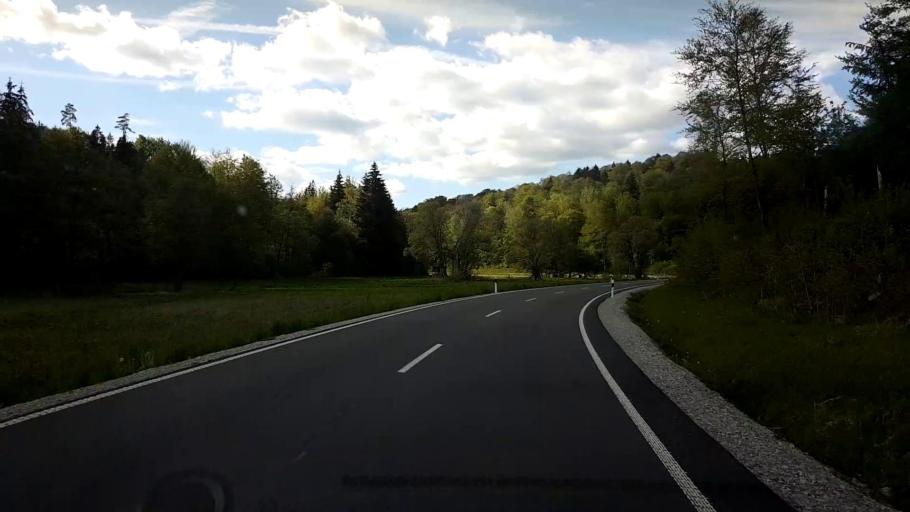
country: DE
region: Bavaria
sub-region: Upper Franconia
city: Hollfeld
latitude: 49.9541
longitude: 11.2632
